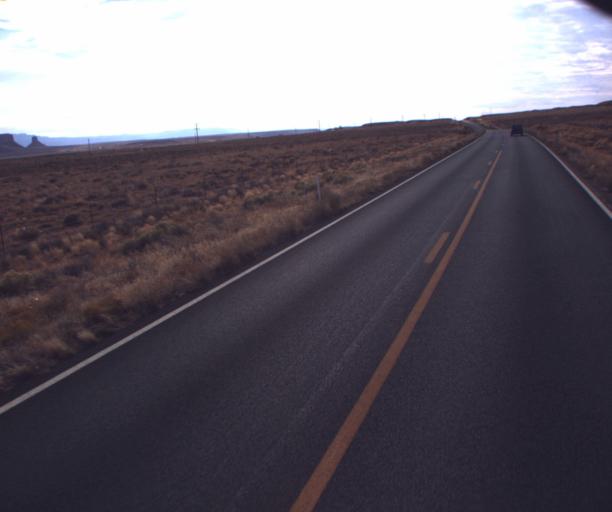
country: US
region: Arizona
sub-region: Apache County
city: Many Farms
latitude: 36.6134
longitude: -109.5785
